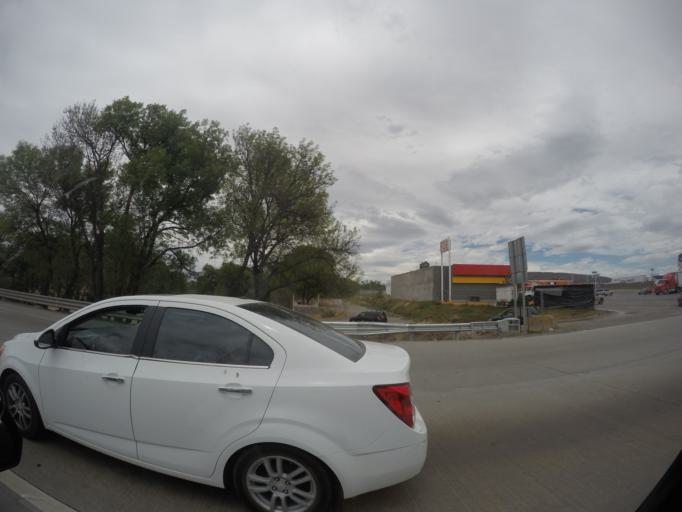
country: MX
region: Hidalgo
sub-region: Tepeji del Rio de Ocampo
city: Santiago Tlautla
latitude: 19.9848
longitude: -99.4406
